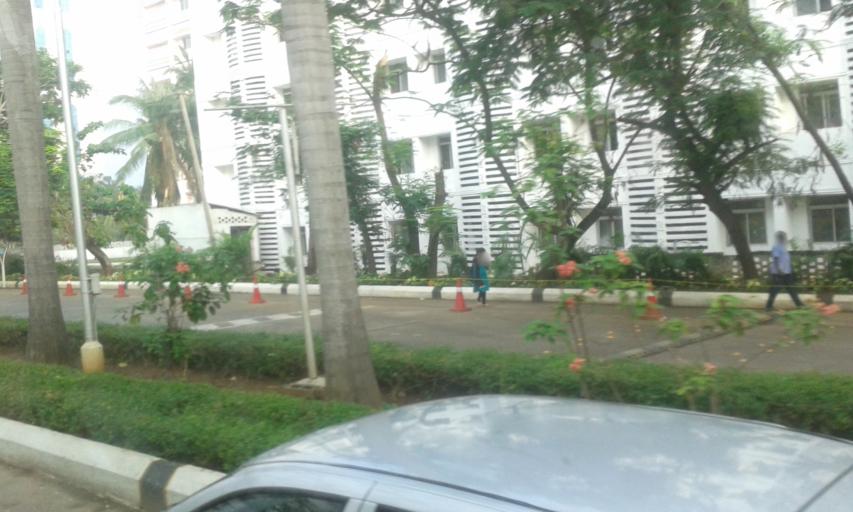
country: IN
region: Tamil Nadu
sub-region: Kancheepuram
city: Guduvancheri
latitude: 12.8229
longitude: 80.0442
